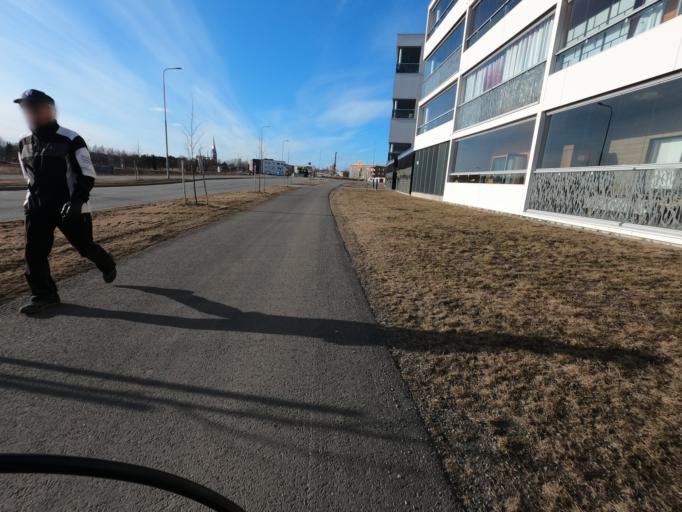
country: FI
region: North Karelia
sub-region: Joensuu
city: Joensuu
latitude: 62.5906
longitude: 29.7601
